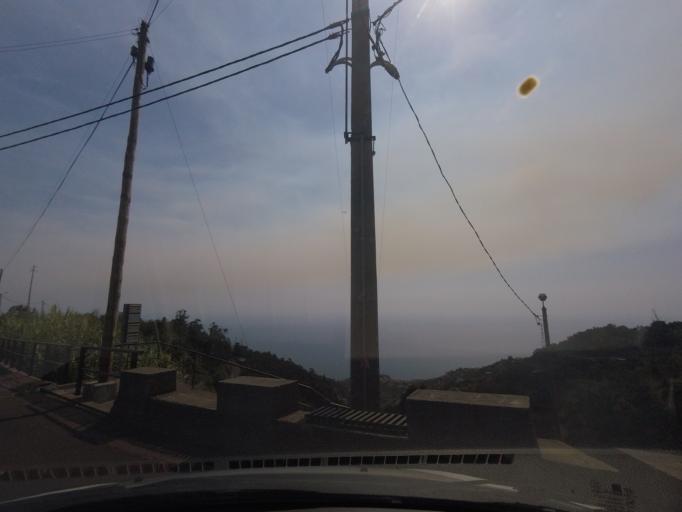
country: PT
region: Madeira
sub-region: Ribeira Brava
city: Campanario
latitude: 32.6922
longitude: -17.0570
